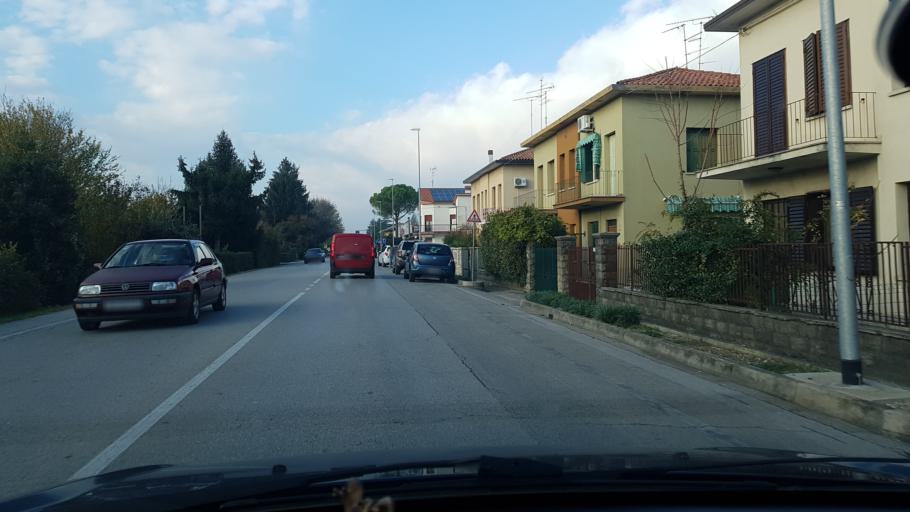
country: IT
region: Friuli Venezia Giulia
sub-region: Provincia di Gorizia
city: Ronchi dei Legionari
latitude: 45.8325
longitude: 13.4992
